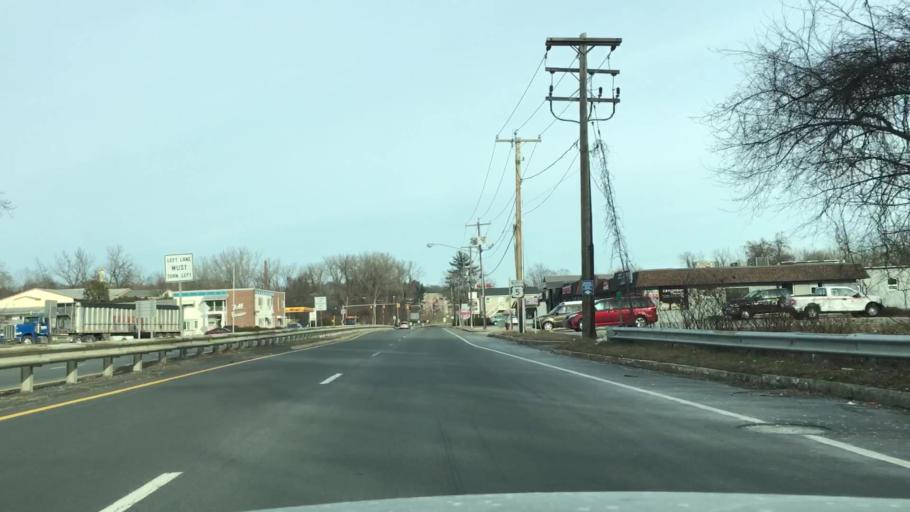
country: US
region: Massachusetts
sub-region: Hampden County
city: Chicopee
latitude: 42.1570
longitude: -72.6327
